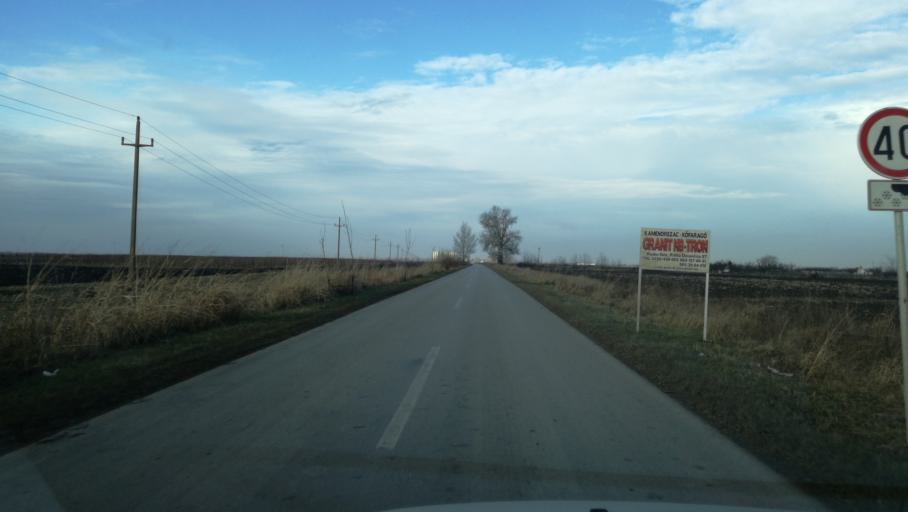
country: RS
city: Novi Kozarci
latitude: 45.7854
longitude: 20.6213
